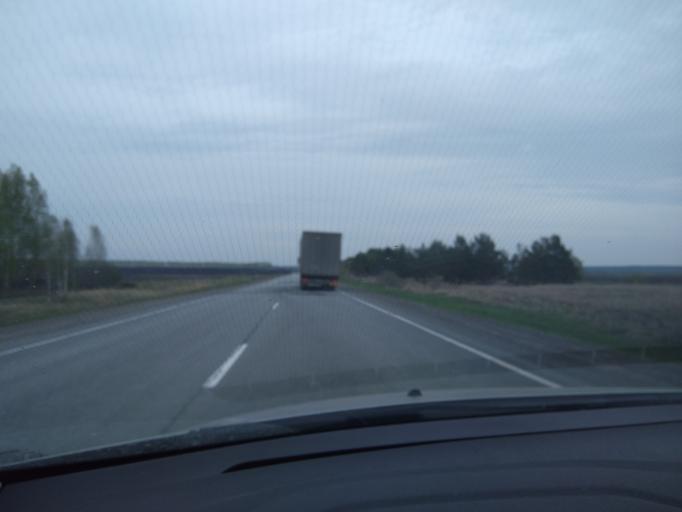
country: RU
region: Sverdlovsk
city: Yelanskiy
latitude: 56.7693
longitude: 62.4361
